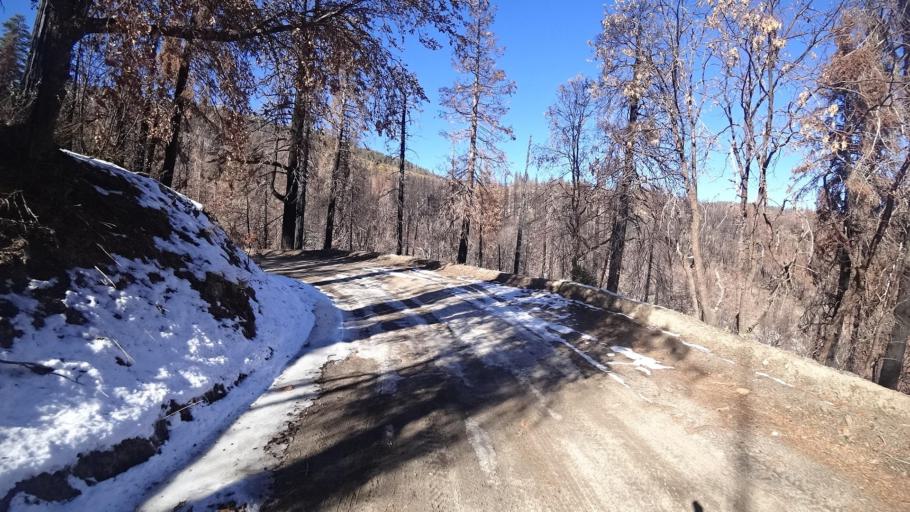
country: US
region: California
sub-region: Kern County
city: Alta Sierra
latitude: 35.7165
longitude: -118.5419
